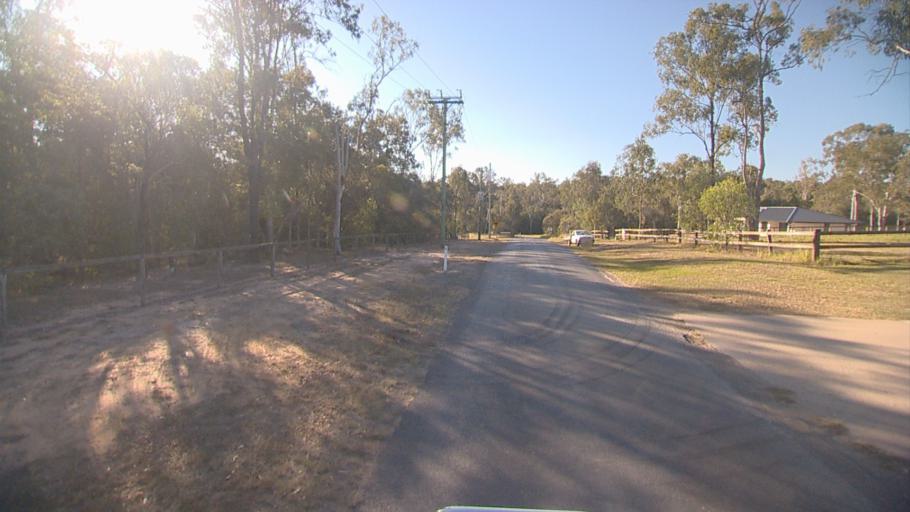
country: AU
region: Queensland
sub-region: Logan
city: North Maclean
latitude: -27.8113
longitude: 153.0410
